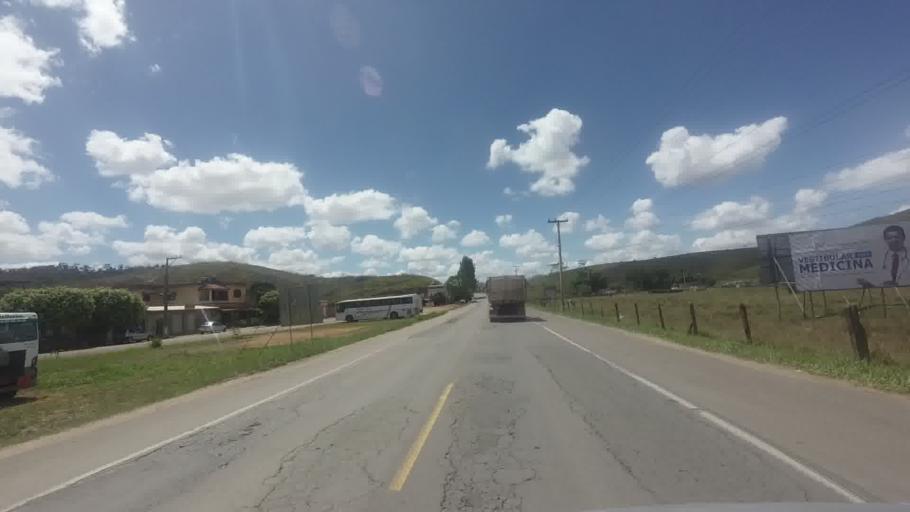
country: BR
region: Minas Gerais
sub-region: Recreio
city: Recreio
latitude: -21.6585
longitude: -42.3331
